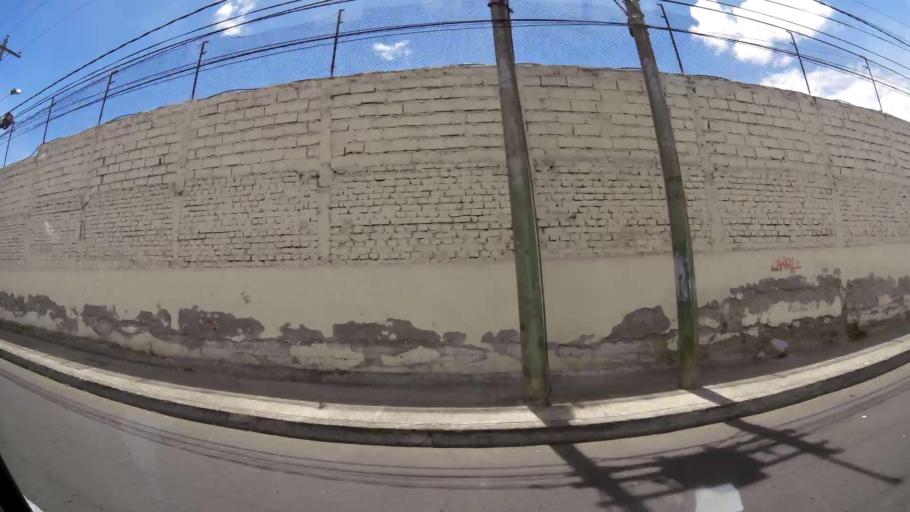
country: EC
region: Tungurahua
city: Ambato
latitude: -1.2672
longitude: -78.6089
